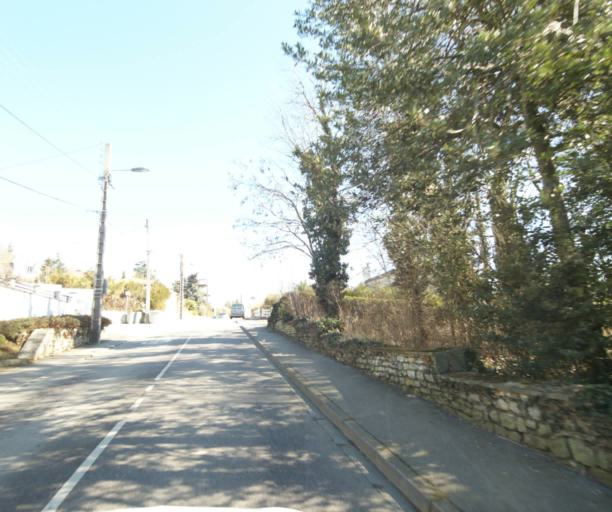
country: FR
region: Lorraine
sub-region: Departement de Meurthe-et-Moselle
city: Saint-Max
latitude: 48.7103
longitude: 6.1984
